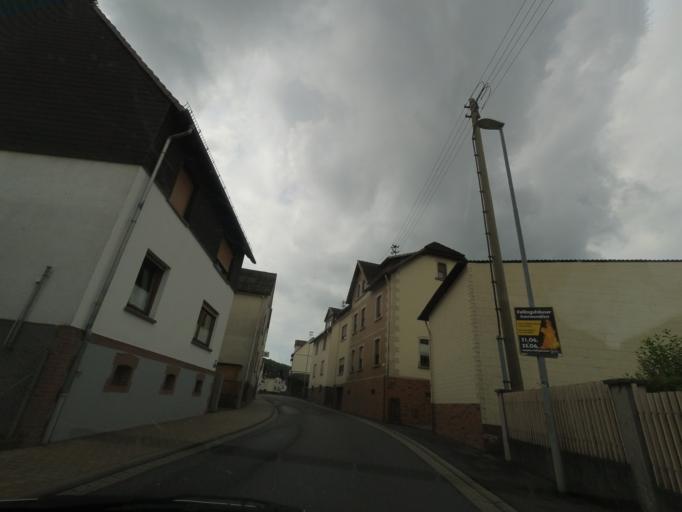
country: DE
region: Hesse
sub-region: Regierungsbezirk Giessen
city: Lohra
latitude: 50.6707
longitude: 8.6002
